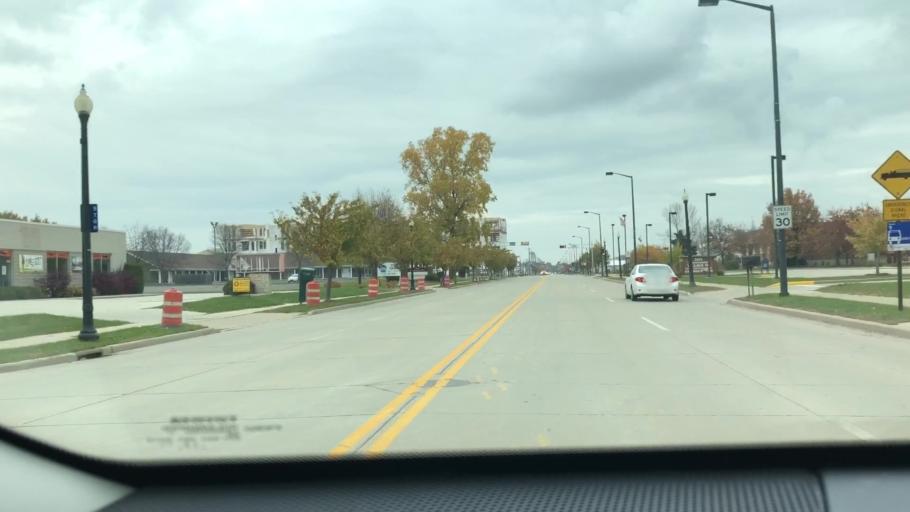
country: US
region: Wisconsin
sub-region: Brown County
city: Ashwaubenon
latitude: 44.4910
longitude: -88.0581
